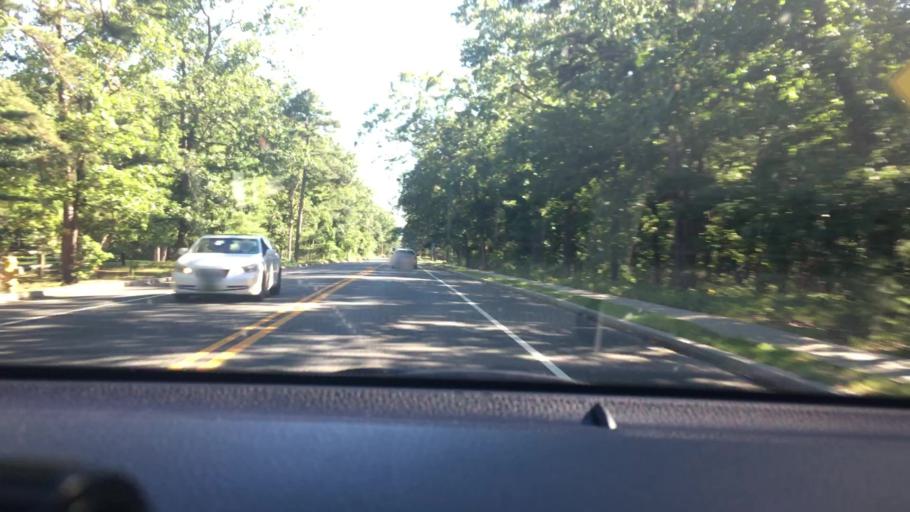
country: US
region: New Jersey
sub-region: Cumberland County
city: Millville
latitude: 39.4139
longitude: -75.0426
